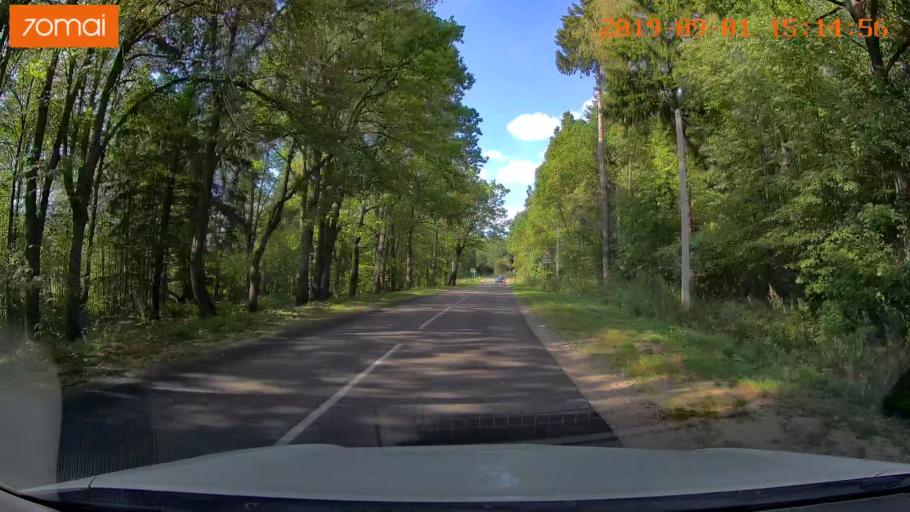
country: RU
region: Kaluga
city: Maloyaroslavets
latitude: 54.8759
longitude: 36.5443
